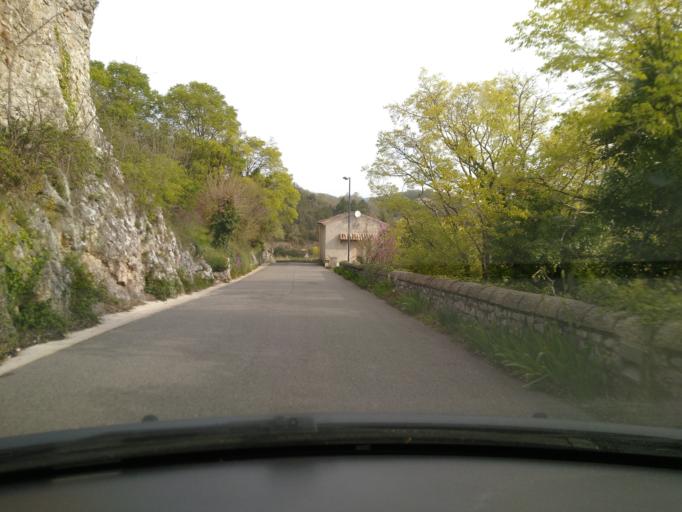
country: FR
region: Rhone-Alpes
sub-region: Departement de l'Ardeche
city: Ruoms
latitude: 44.4507
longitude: 4.4173
